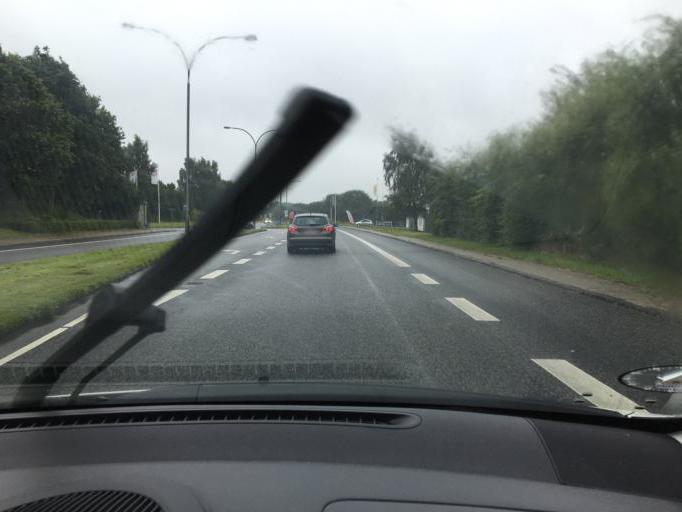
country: DK
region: South Denmark
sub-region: Vejle Kommune
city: Vejle
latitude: 55.6761
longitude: 9.5315
